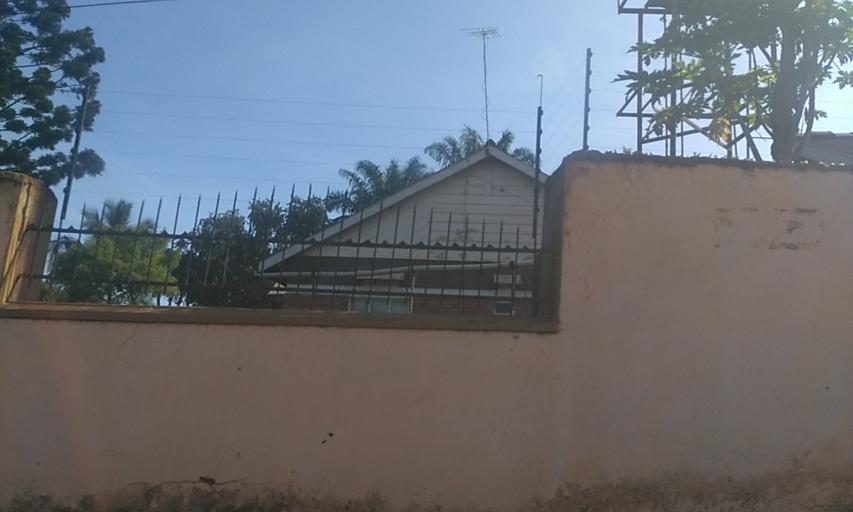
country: UG
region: Central Region
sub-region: Wakiso District
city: Kireka
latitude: 0.3637
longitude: 32.6276
